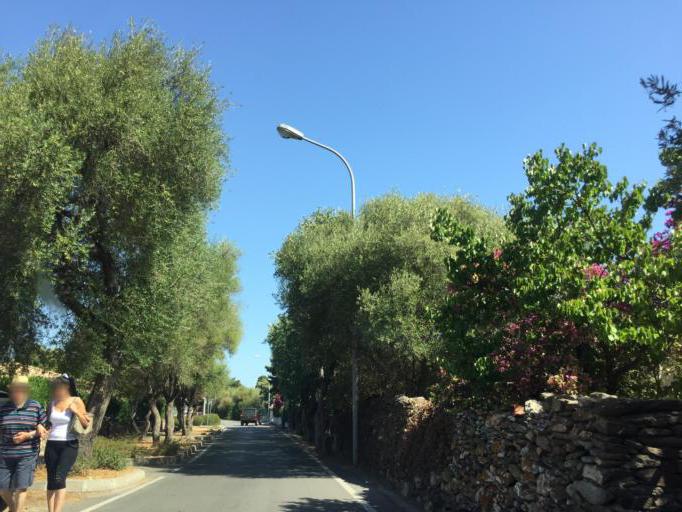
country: IT
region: Sardinia
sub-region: Provincia di Olbia-Tempio
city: San Teodoro
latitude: 40.7740
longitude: 9.6707
